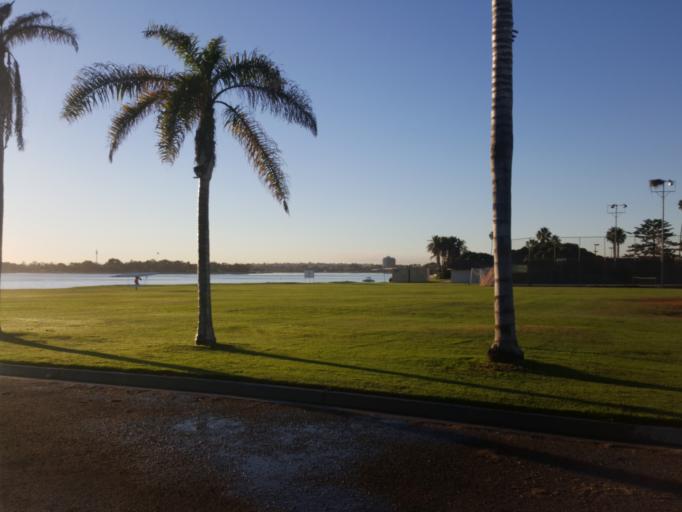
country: US
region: California
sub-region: San Diego County
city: La Jolla
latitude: 32.7847
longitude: -117.2494
